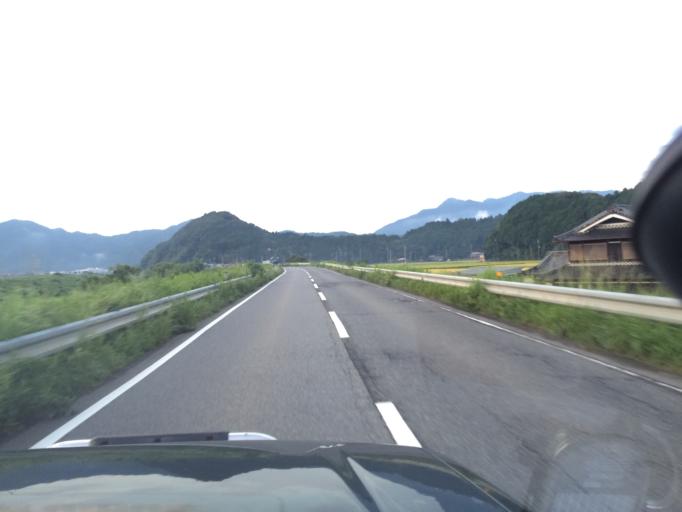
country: JP
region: Hyogo
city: Nishiwaki
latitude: 35.1453
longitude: 135.0332
